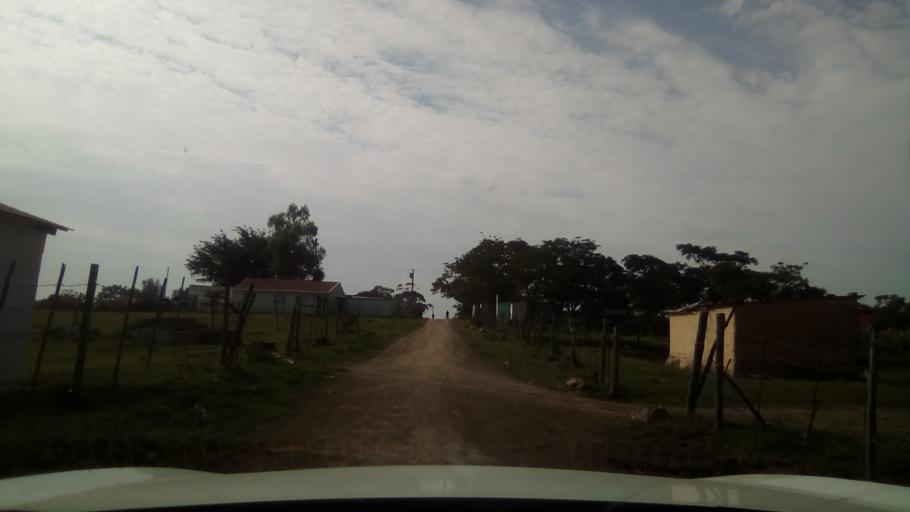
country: ZA
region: Eastern Cape
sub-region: Buffalo City Metropolitan Municipality
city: Bhisho
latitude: -33.0071
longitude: 27.2997
